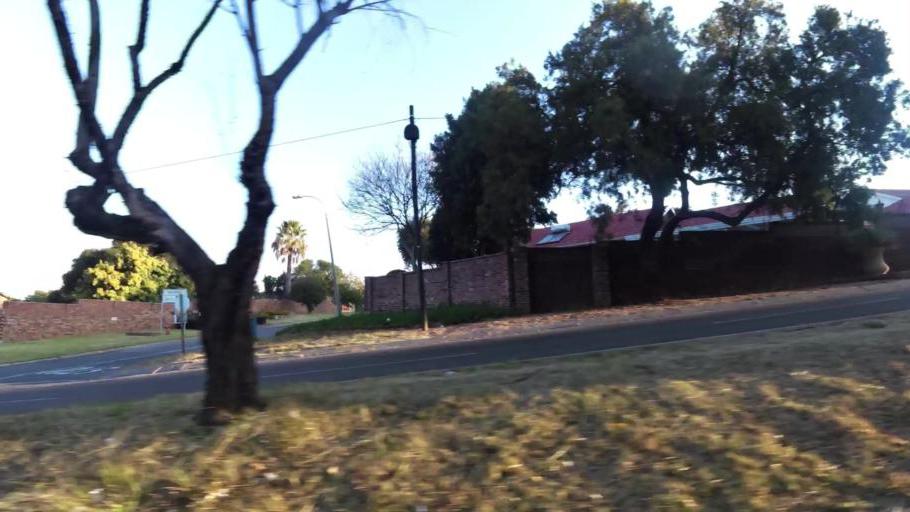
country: ZA
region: Gauteng
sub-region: City of Johannesburg Metropolitan Municipality
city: Roodepoort
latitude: -26.1659
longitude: 27.9575
